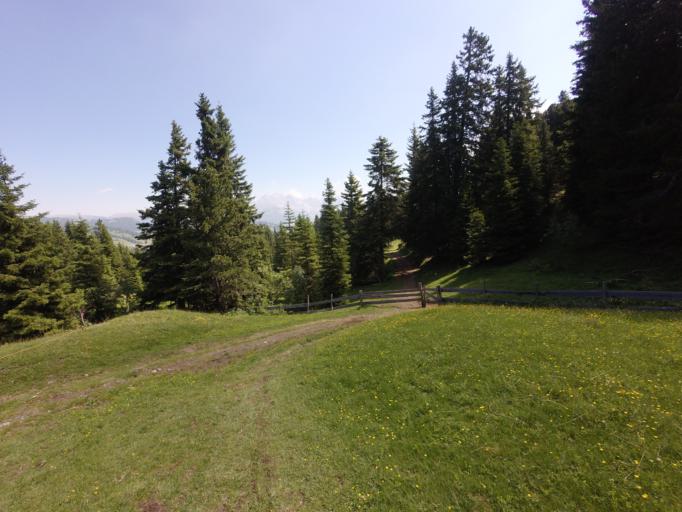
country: IT
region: Trentino-Alto Adige
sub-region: Bolzano
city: Ortisei
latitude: 46.5204
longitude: 11.6543
